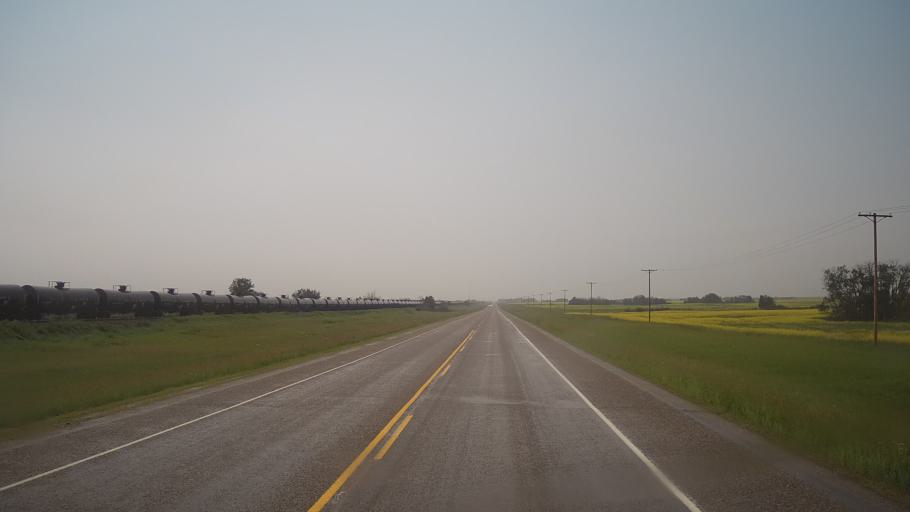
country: CA
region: Saskatchewan
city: Biggar
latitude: 52.1617
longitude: -108.2837
